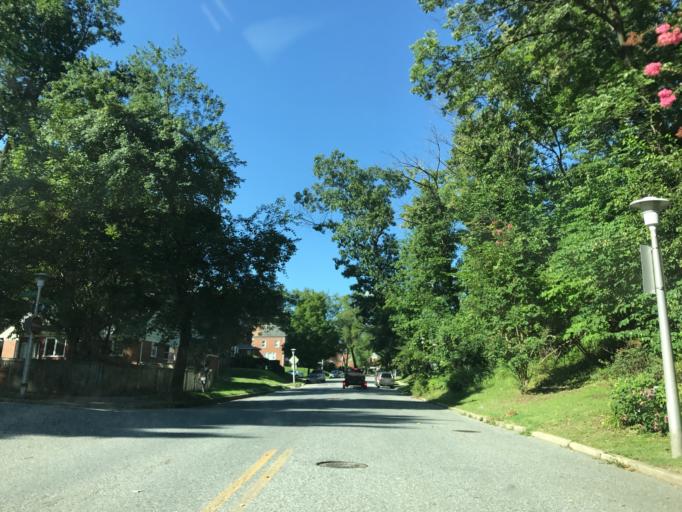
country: US
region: Maryland
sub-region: Baltimore County
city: Charlestown
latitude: 39.2965
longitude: -76.7027
